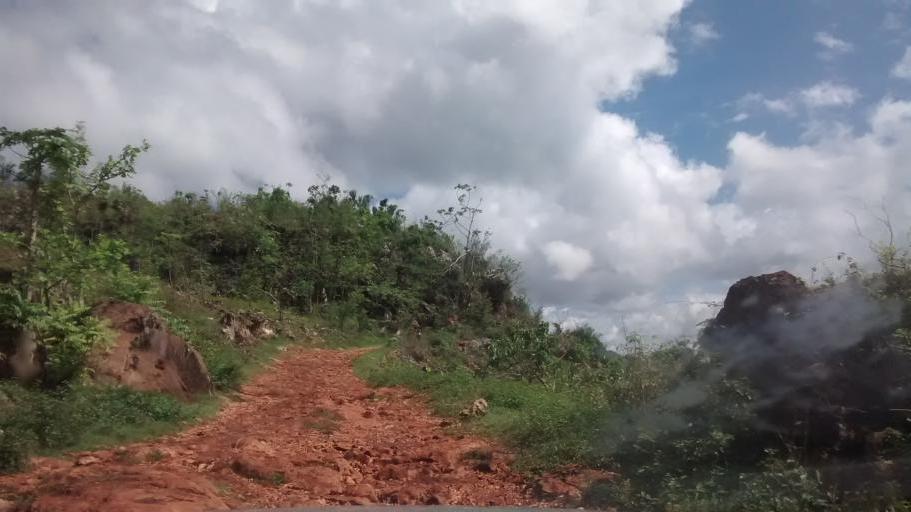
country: HT
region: Grandans
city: Corail
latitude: 18.5399
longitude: -73.9211
